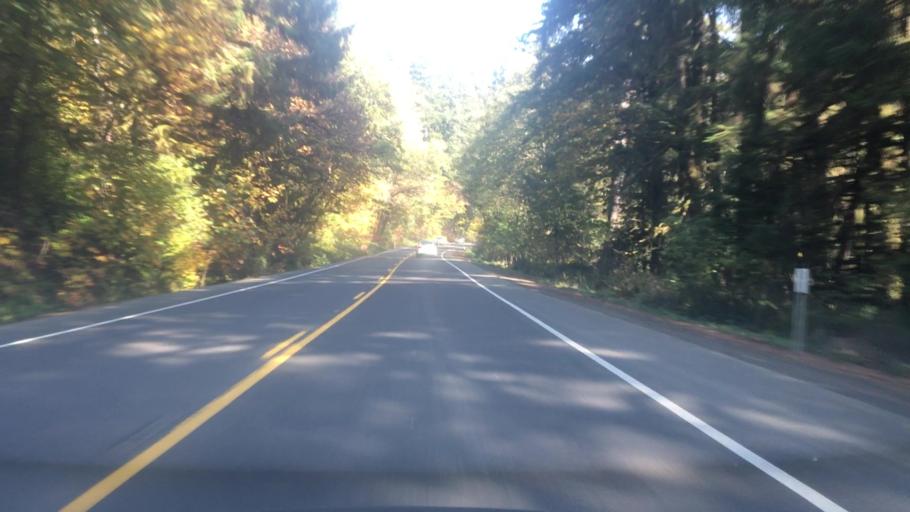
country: US
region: Oregon
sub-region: Lincoln County
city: Rose Lodge
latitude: 45.0515
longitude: -123.7794
